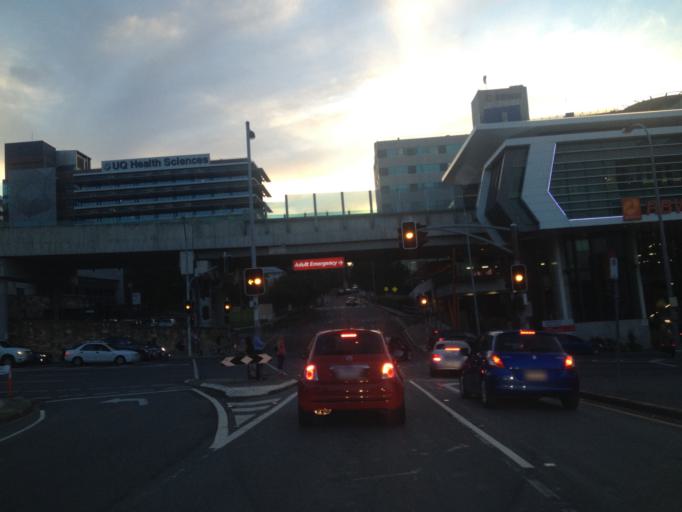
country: AU
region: Queensland
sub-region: Brisbane
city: Fortitude Valley
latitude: -27.4479
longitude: 153.0297
